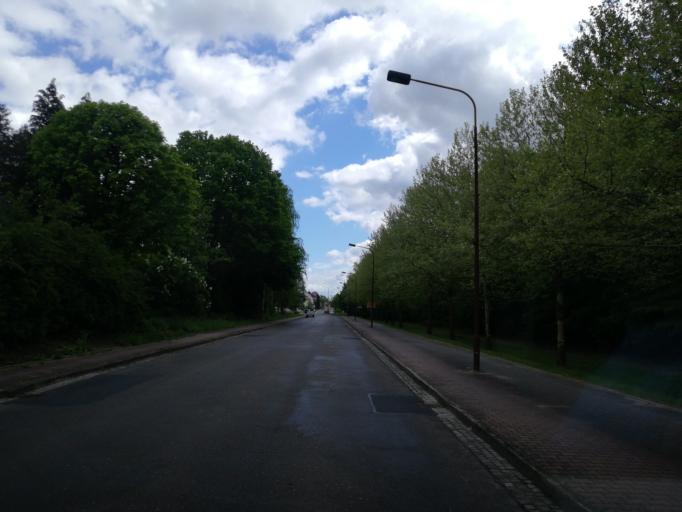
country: DE
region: Brandenburg
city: Lauchhammer
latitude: 51.4972
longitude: 13.7792
